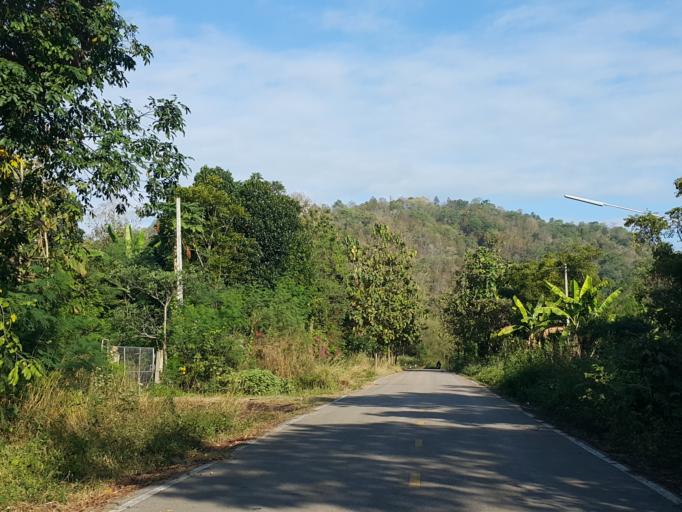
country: TH
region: Lampang
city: Mae Mo
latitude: 18.2640
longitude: 99.6311
